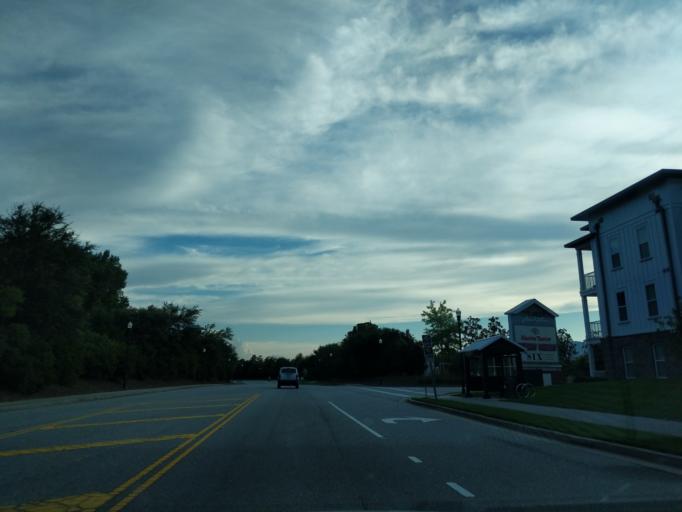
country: US
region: South Carolina
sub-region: Charleston County
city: Isle of Palms
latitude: 32.8382
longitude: -79.8150
